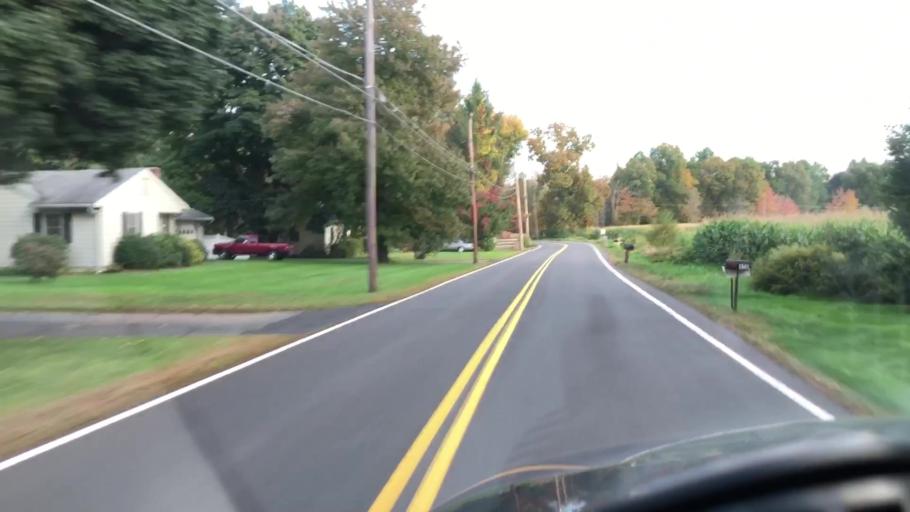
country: US
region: Connecticut
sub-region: Hartford County
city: Suffield Depot
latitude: 42.0174
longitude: -72.6571
